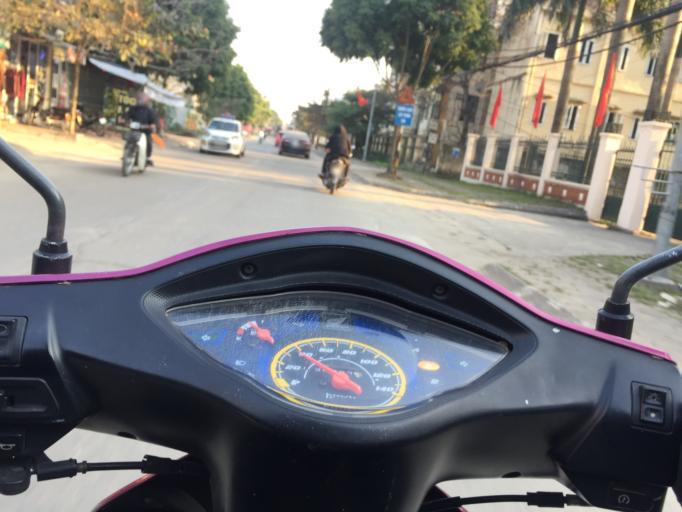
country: VN
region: Ha Noi
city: Chuc Son
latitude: 20.9200
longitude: 105.7126
